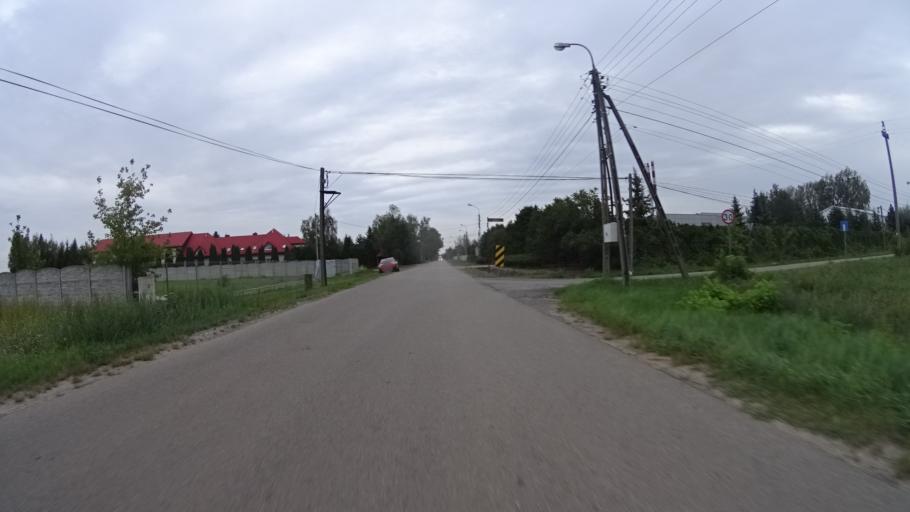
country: PL
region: Masovian Voivodeship
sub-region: Powiat warszawski zachodni
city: Ozarow Mazowiecki
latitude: 52.2470
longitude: 20.7878
